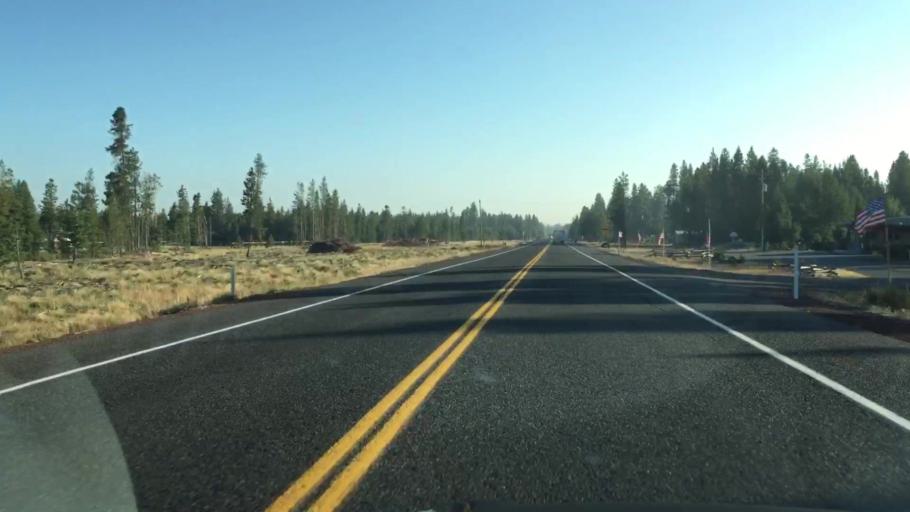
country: US
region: Oregon
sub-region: Deschutes County
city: La Pine
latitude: 43.4485
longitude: -121.7062
